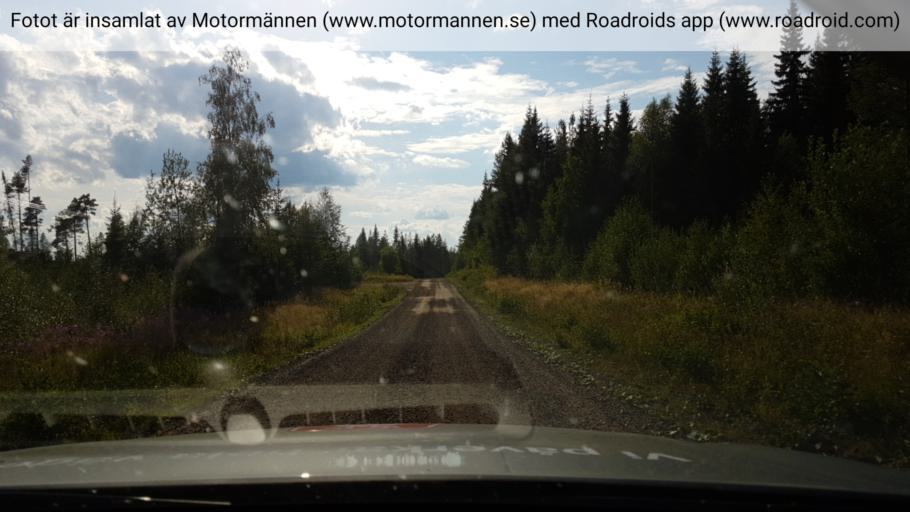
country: SE
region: Jaemtland
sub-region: Stroemsunds Kommun
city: Stroemsund
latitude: 63.7206
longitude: 16.0504
